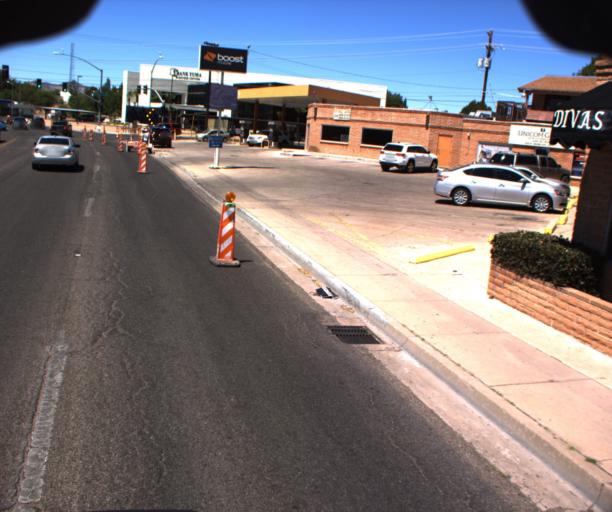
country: US
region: Arizona
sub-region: Santa Cruz County
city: Nogales
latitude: 31.3482
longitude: -110.9296
